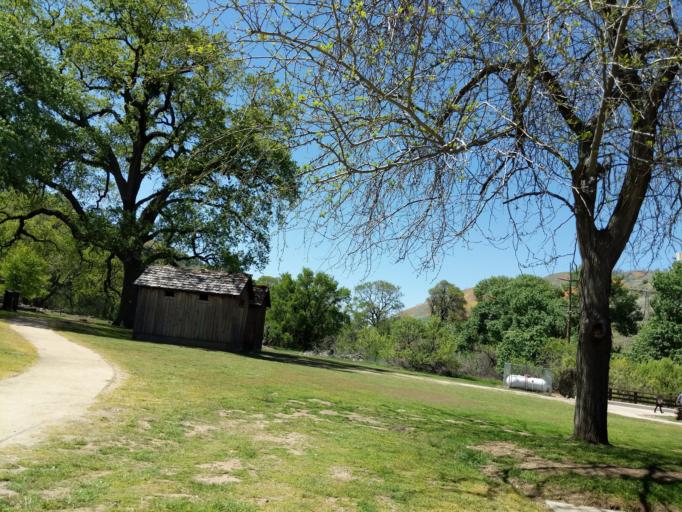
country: US
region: California
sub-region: Kern County
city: Lebec
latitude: 34.8745
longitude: -118.8934
